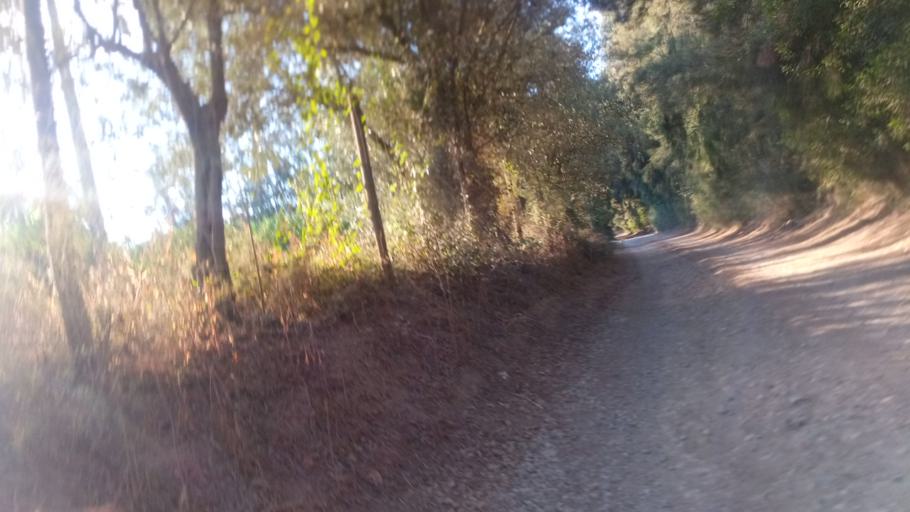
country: PT
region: Faro
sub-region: Tavira
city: Tavira
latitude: 37.1533
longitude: -7.5747
